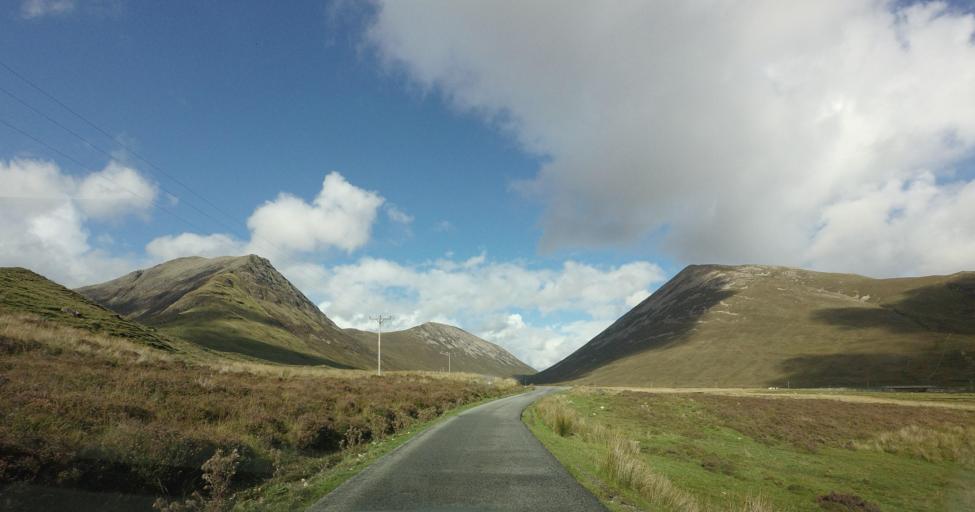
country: GB
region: Scotland
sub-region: Highland
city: Portree
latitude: 57.2244
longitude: -6.0414
